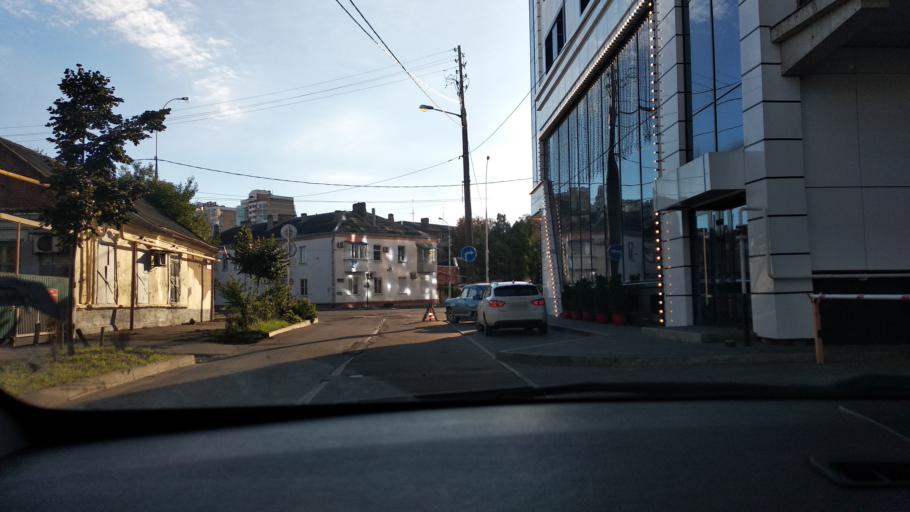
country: RU
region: Krasnodarskiy
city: Krasnodar
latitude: 45.0209
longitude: 38.9808
